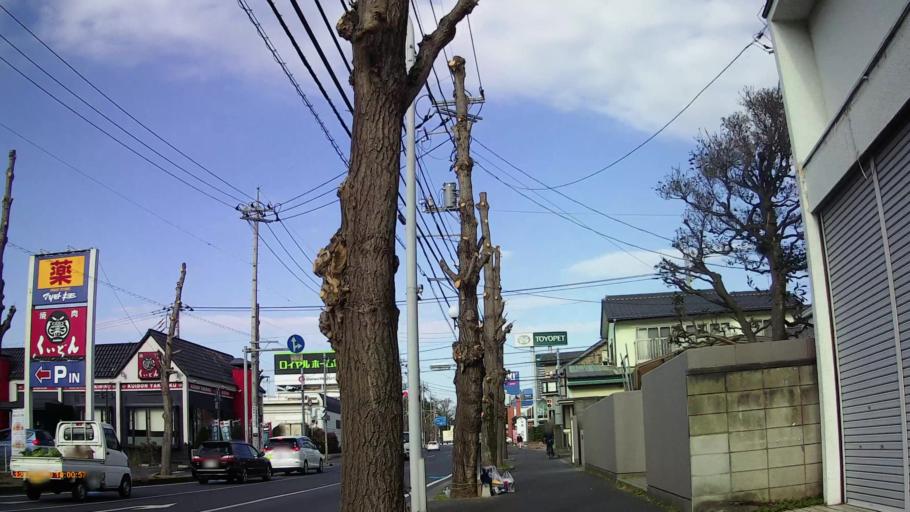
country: JP
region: Chiba
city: Yotsukaido
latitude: 35.6335
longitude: 140.1664
